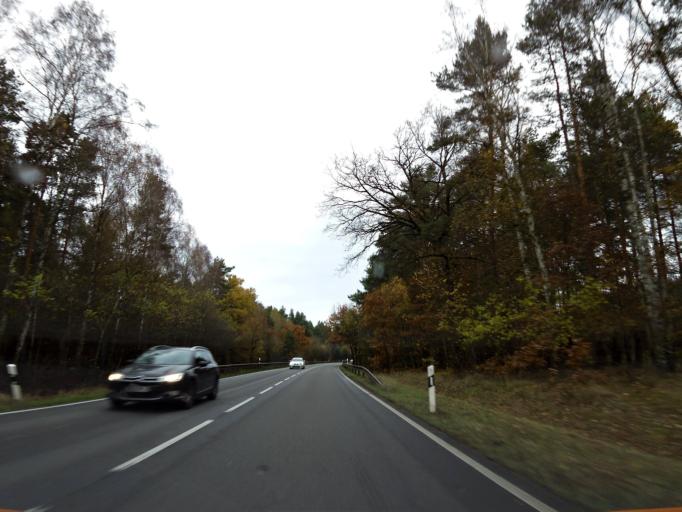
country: DE
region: Saxony-Anhalt
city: Haldensleben I
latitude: 52.3536
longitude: 11.4509
